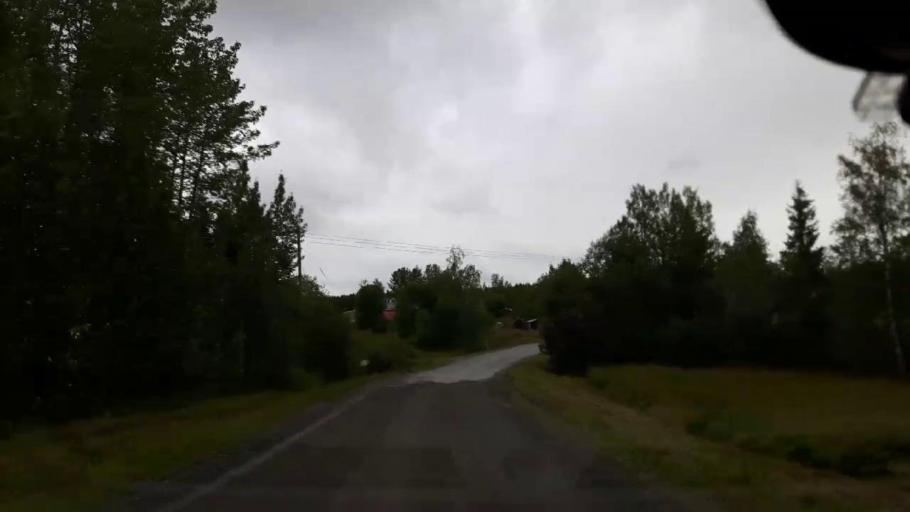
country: SE
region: Jaemtland
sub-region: OEstersunds Kommun
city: Ostersund
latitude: 63.0149
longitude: 14.5888
